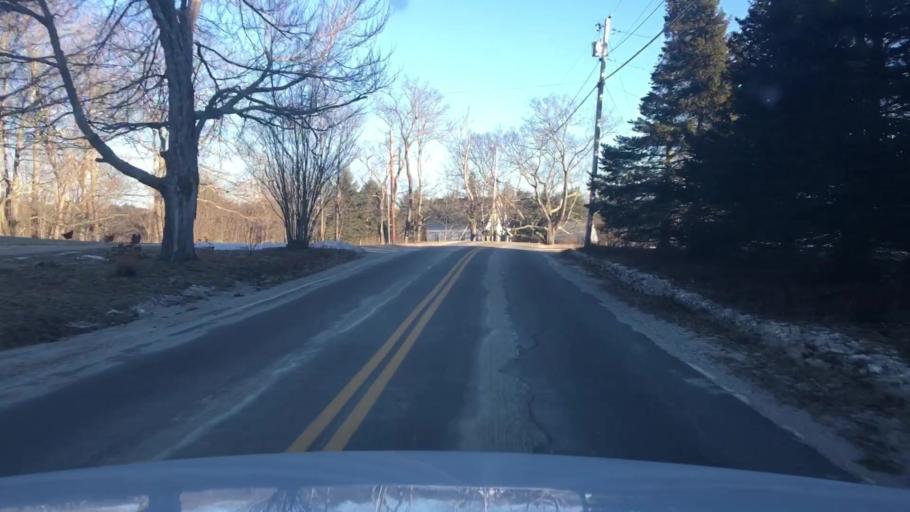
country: US
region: Maine
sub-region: Hancock County
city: Penobscot
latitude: 44.3892
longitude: -68.7002
